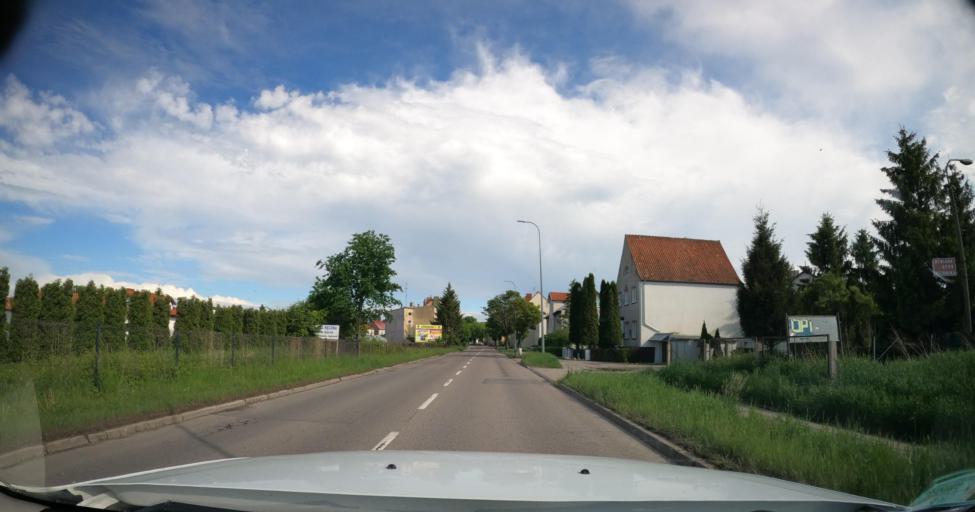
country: PL
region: Warmian-Masurian Voivodeship
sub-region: Powiat elblaski
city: Elblag
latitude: 54.1616
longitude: 19.3831
